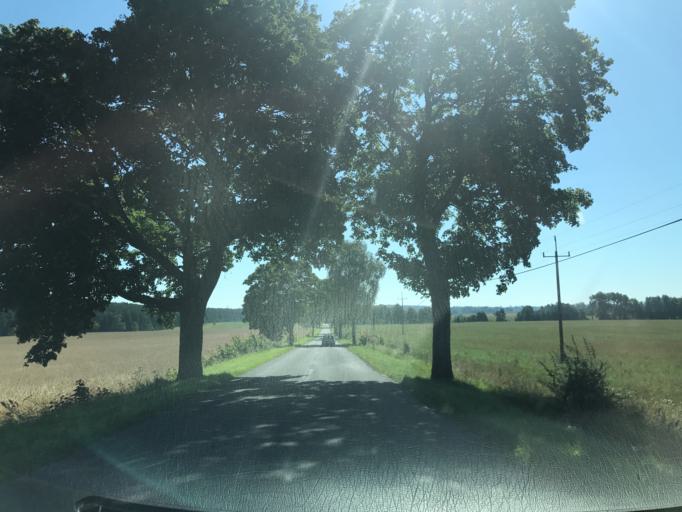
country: PL
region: Pomeranian Voivodeship
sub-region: Powiat bytowski
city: Czarna Dabrowka
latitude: 54.3618
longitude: 17.5263
